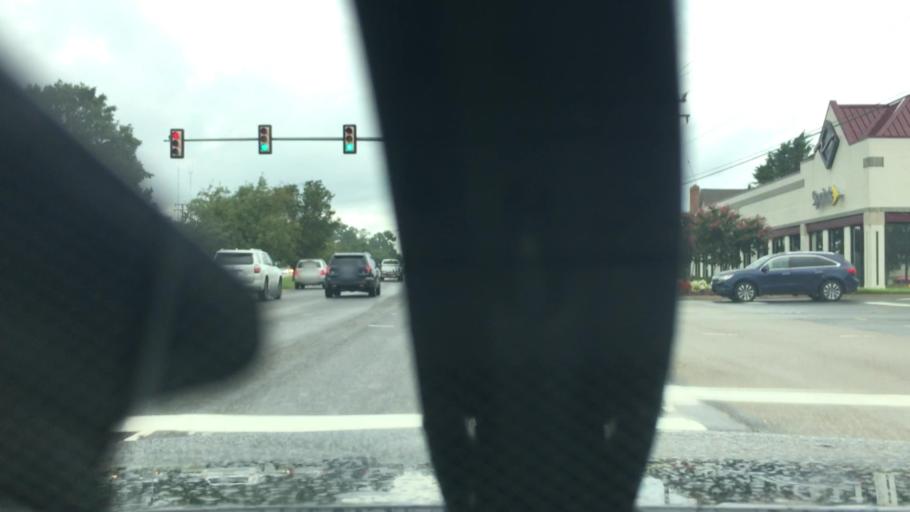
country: US
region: Virginia
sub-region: Chesterfield County
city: Bon Air
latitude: 37.5037
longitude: -77.5761
